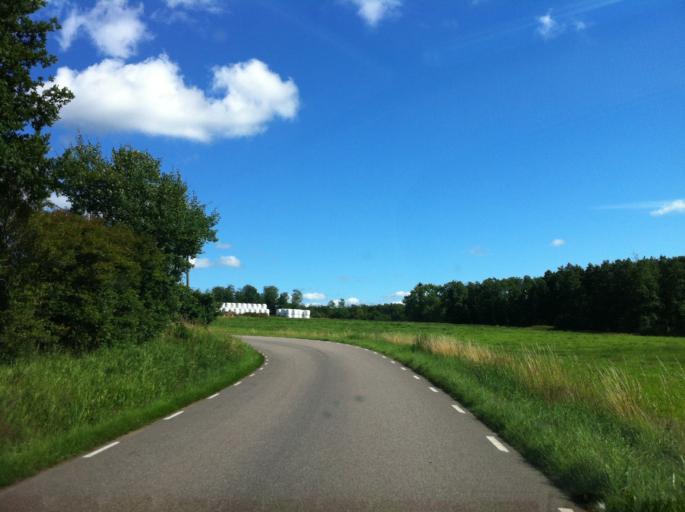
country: SE
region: Skane
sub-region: Svalovs Kommun
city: Kagerod
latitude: 56.0699
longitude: 13.0766
